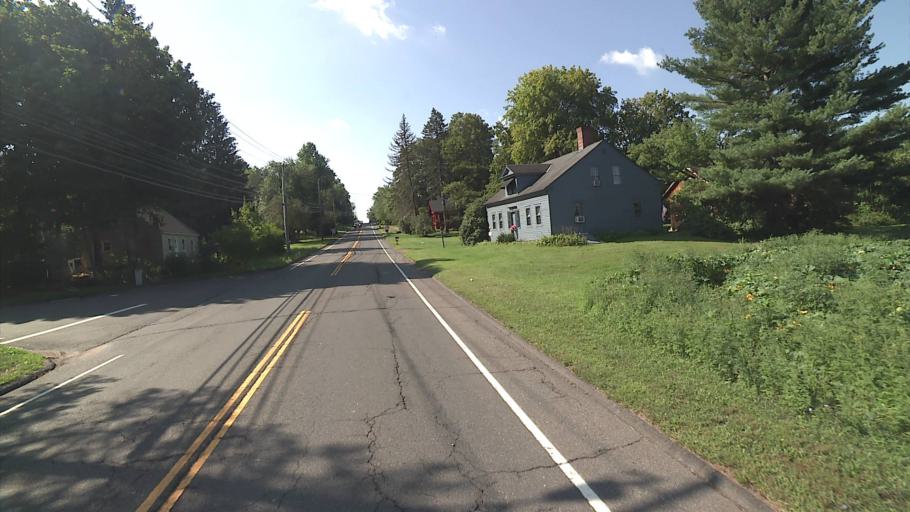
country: US
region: Connecticut
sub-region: Hartford County
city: Thompsonville
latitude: 41.9942
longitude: -72.6139
